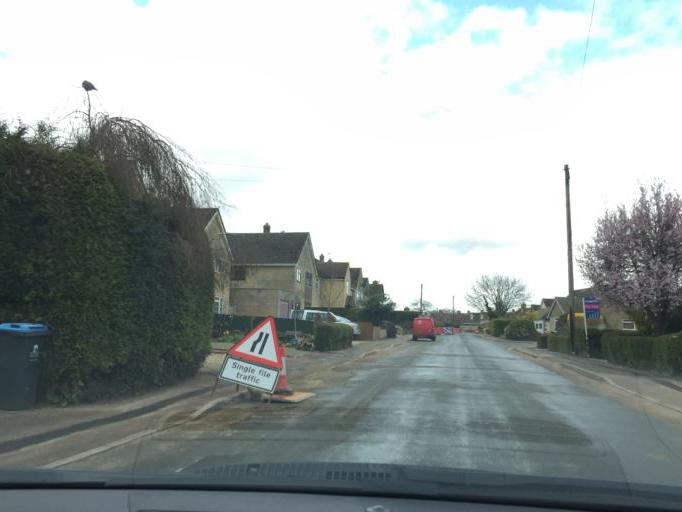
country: GB
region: England
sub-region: Oxfordshire
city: Stonesfield
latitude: 51.8528
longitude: -1.4265
